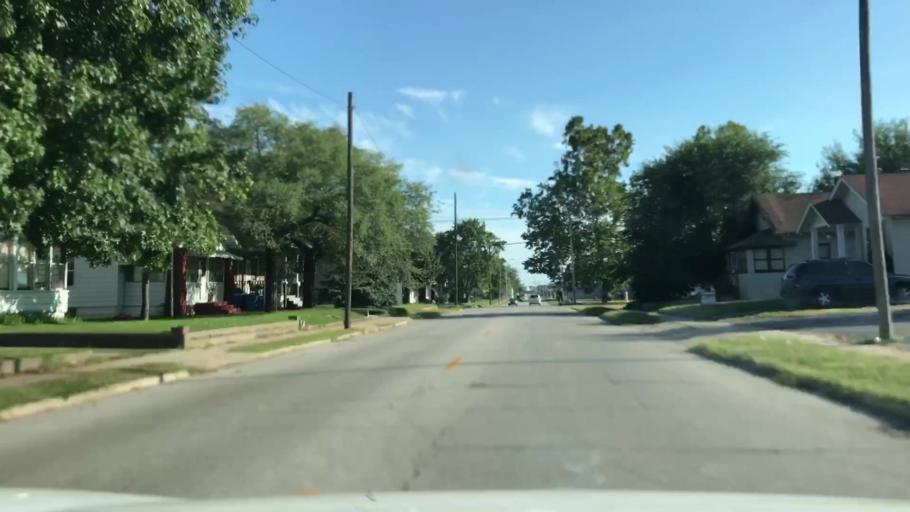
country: US
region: Illinois
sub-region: Madison County
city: Wood River
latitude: 38.8669
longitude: -90.0985
